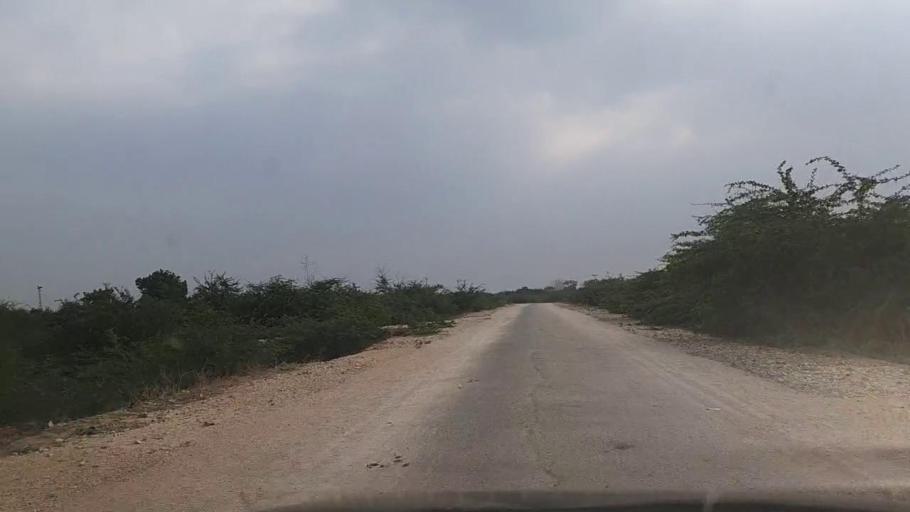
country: PK
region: Sindh
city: Thatta
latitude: 24.8471
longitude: 67.7776
